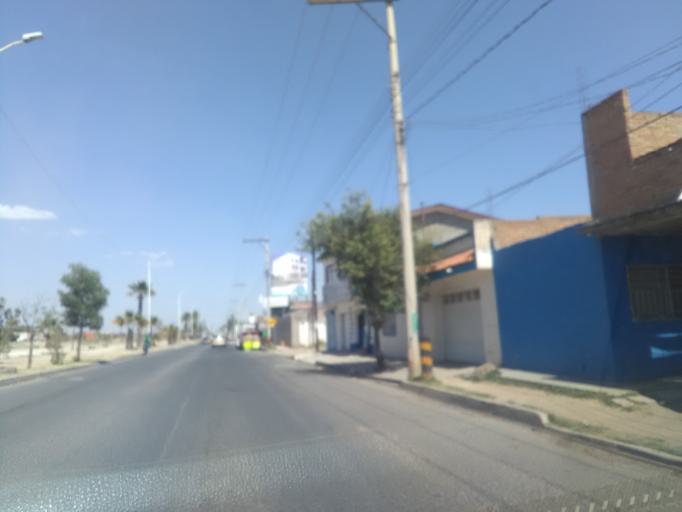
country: MX
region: Durango
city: Victoria de Durango
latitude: 24.0452
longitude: -104.6442
